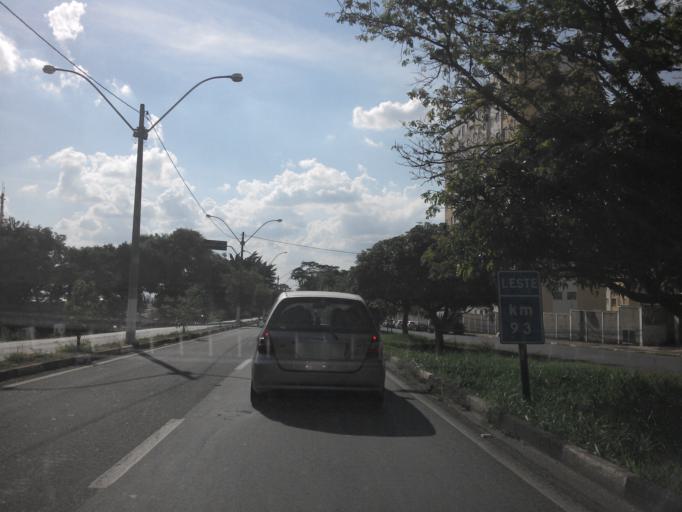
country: BR
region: Sao Paulo
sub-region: Campinas
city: Campinas
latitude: -22.9413
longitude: -47.0333
